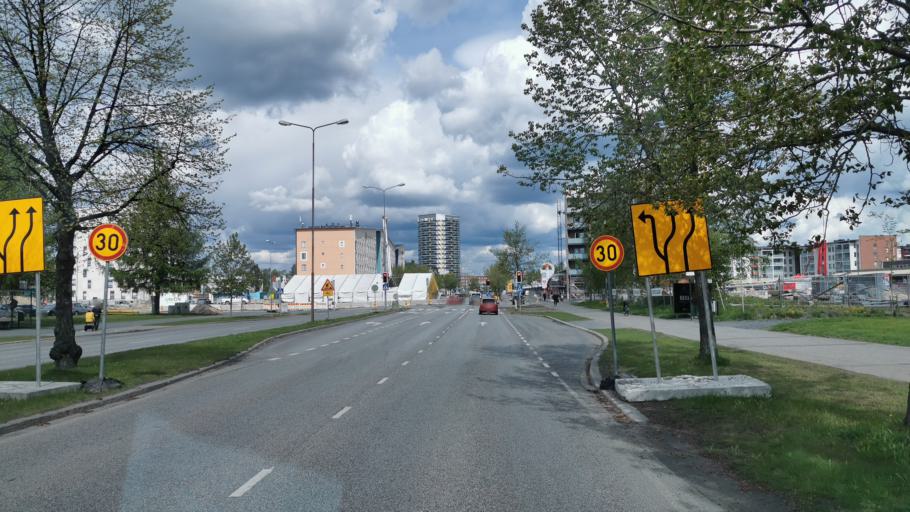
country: FI
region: Northern Ostrobothnia
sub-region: Oulu
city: Oulu
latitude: 64.9997
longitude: 25.4642
